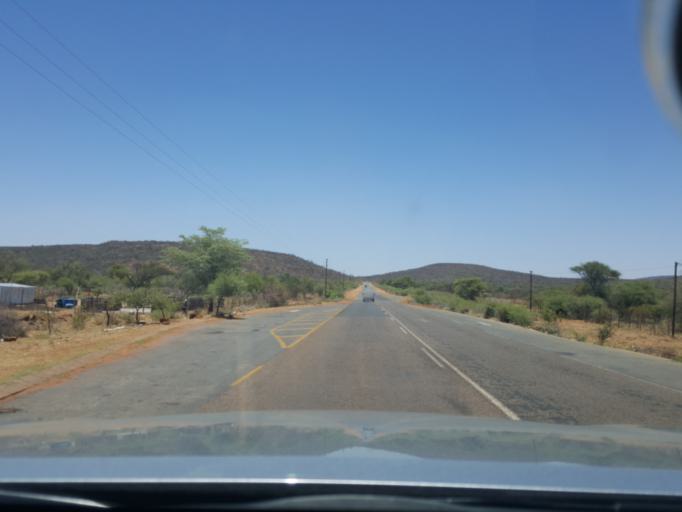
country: ZA
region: North-West
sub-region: Ngaka Modiri Molema District Municipality
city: Zeerust
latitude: -25.3709
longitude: 25.9354
